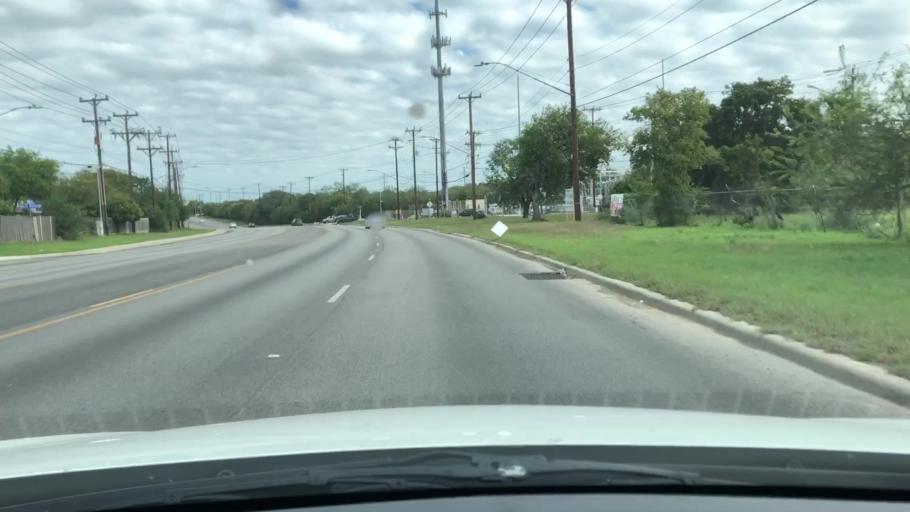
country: US
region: Texas
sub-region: Bexar County
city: Leon Valley
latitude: 29.4770
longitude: -98.6509
